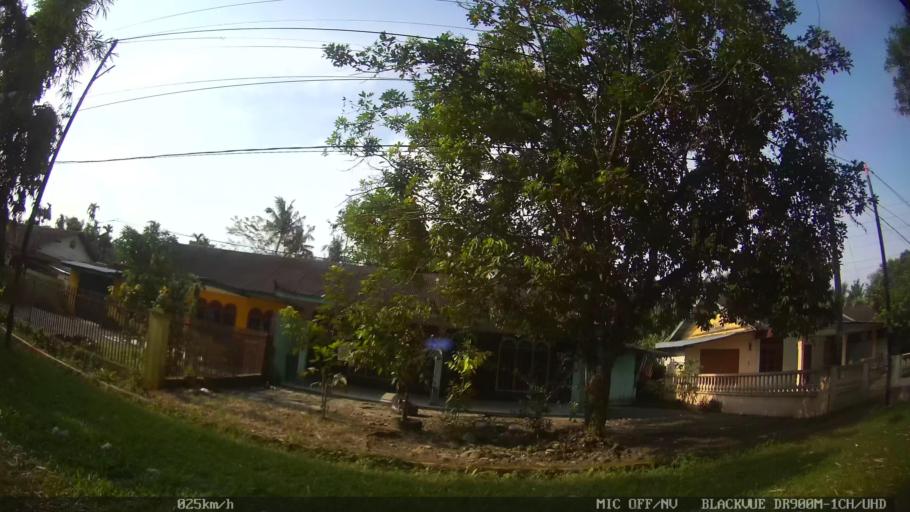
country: ID
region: North Sumatra
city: Binjai
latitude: 3.6031
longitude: 98.5092
